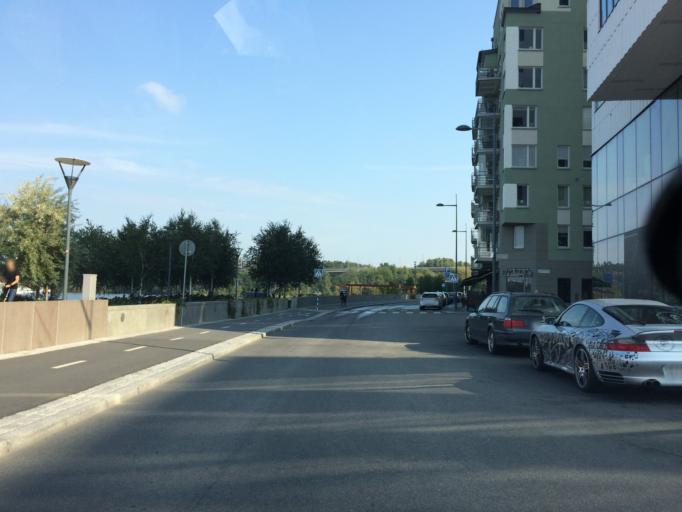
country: SE
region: Stockholm
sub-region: Solna Kommun
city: Solna
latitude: 59.3397
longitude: 18.0050
